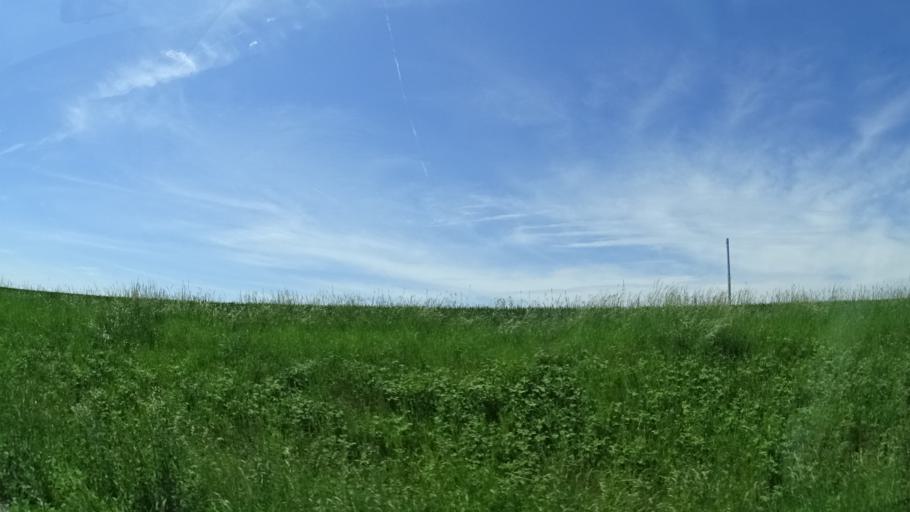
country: DE
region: Bavaria
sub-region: Regierungsbezirk Unterfranken
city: Poppenhausen
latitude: 50.1099
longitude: 10.1440
